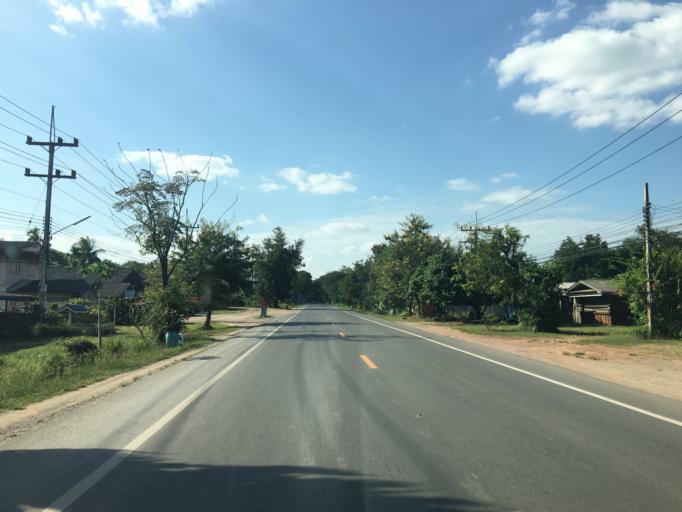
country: TH
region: Phayao
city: Chun
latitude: 19.3457
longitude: 100.1167
